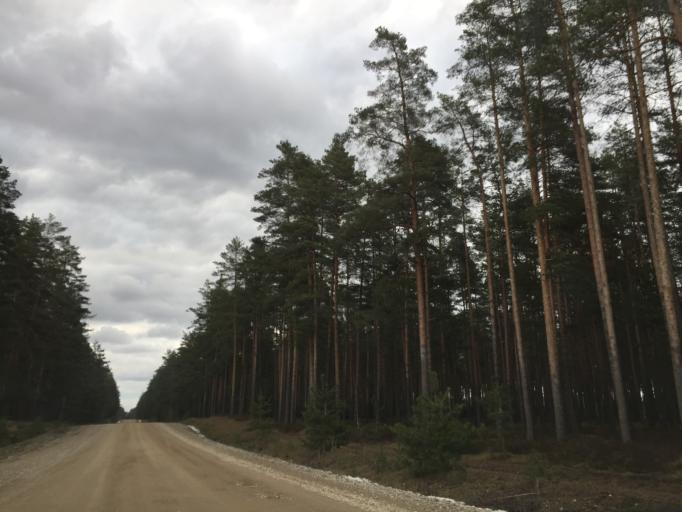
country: LV
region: Jaunjelgava
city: Jaunjelgava
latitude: 56.5802
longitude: 25.0251
